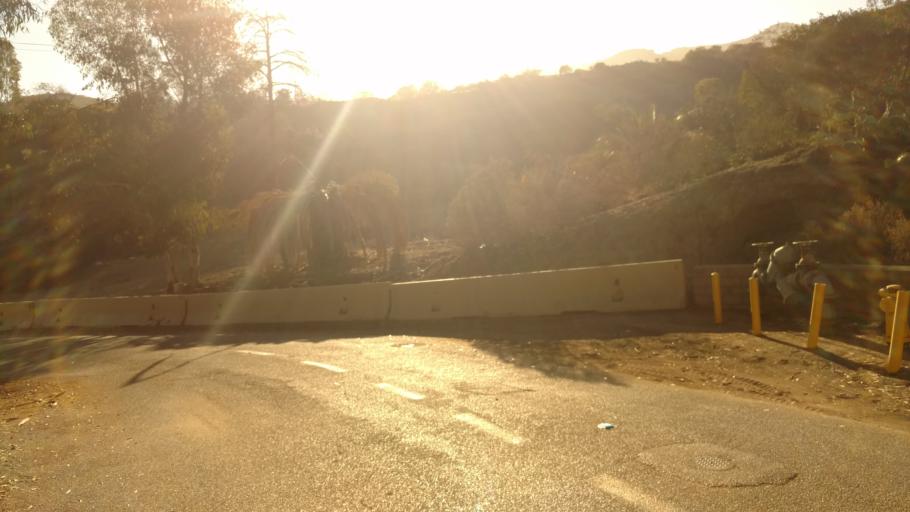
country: US
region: California
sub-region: Los Angeles County
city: Avalon
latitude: 33.3408
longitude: -118.3329
